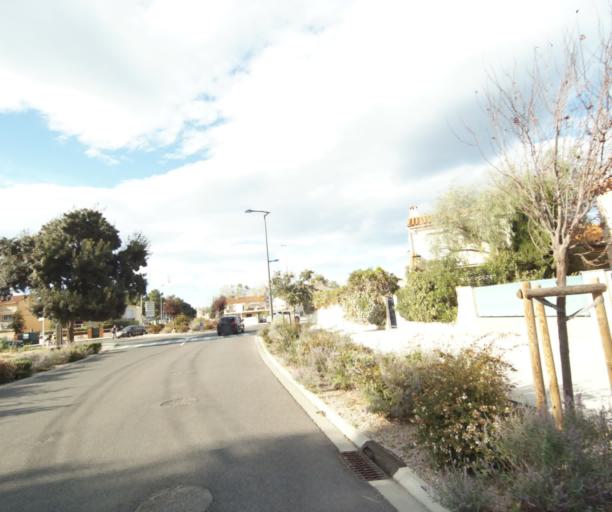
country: FR
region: Languedoc-Roussillon
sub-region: Departement des Pyrenees-Orientales
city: Argelers
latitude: 42.5467
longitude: 3.0341
